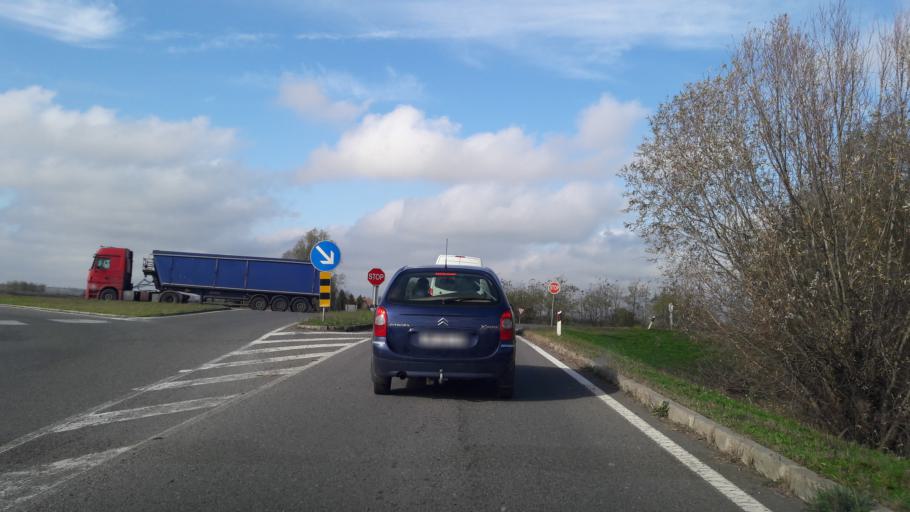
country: HR
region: Osjecko-Baranjska
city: Darda
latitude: 45.6204
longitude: 18.6771
